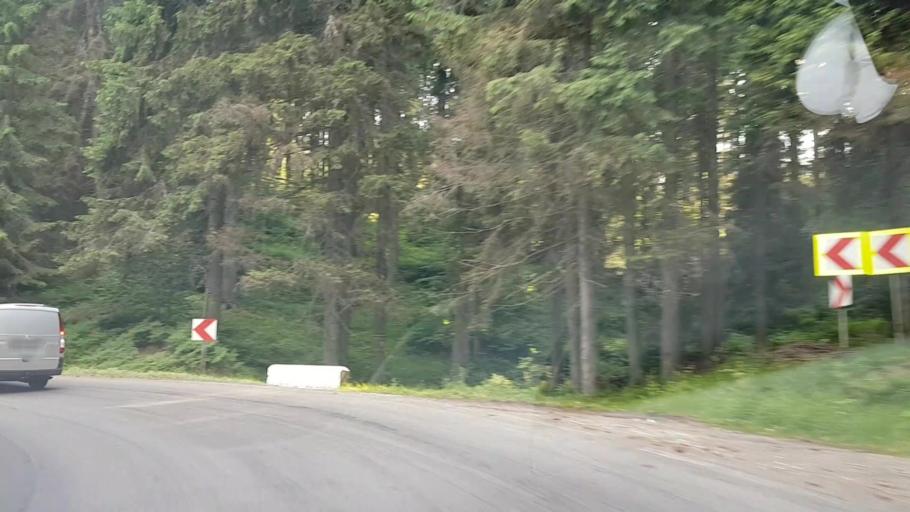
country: RO
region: Harghita
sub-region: Comuna Varsag
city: Varsag
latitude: 46.6616
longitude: 25.3014
